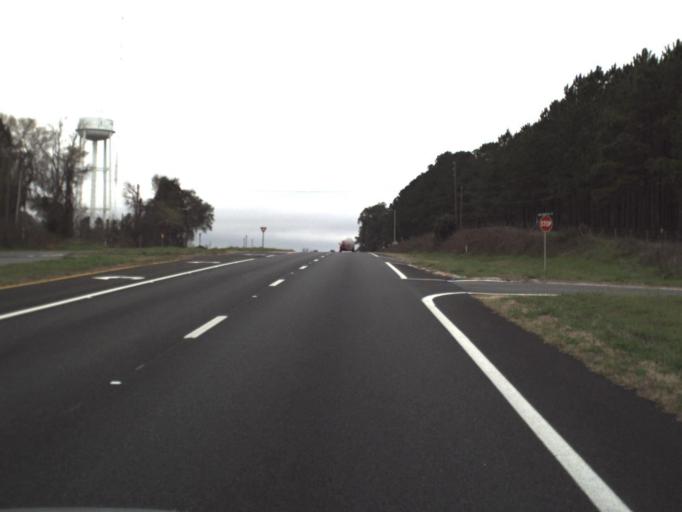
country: US
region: Florida
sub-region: Jefferson County
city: Monticello
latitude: 30.3850
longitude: -83.8304
